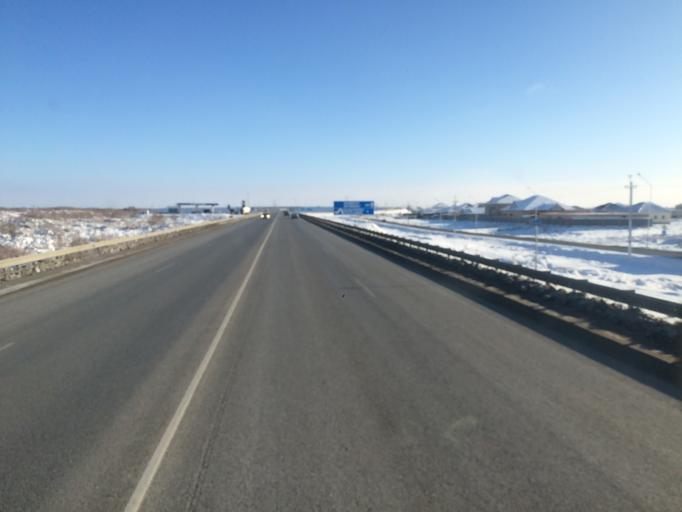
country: KZ
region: Qyzylorda
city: Tasboget
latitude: 44.7776
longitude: 65.4822
